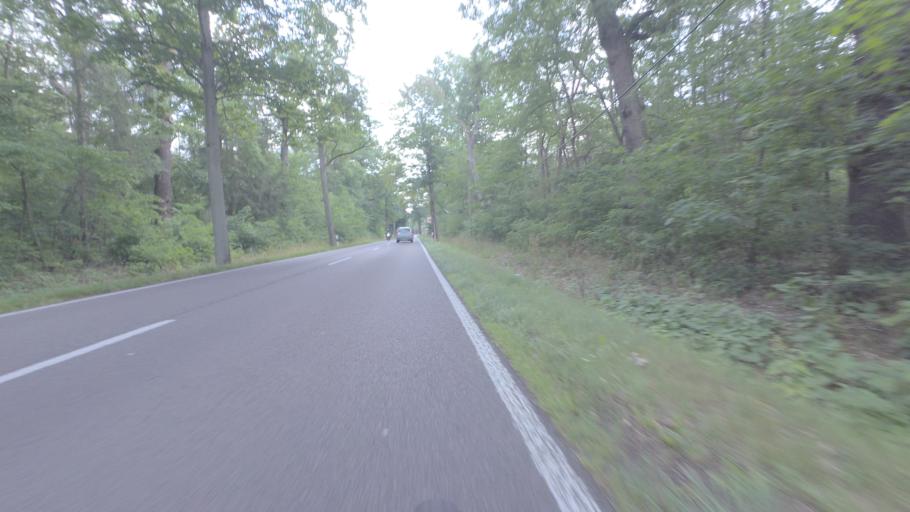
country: DE
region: Brandenburg
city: Sperenberg
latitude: 52.1675
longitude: 13.3252
